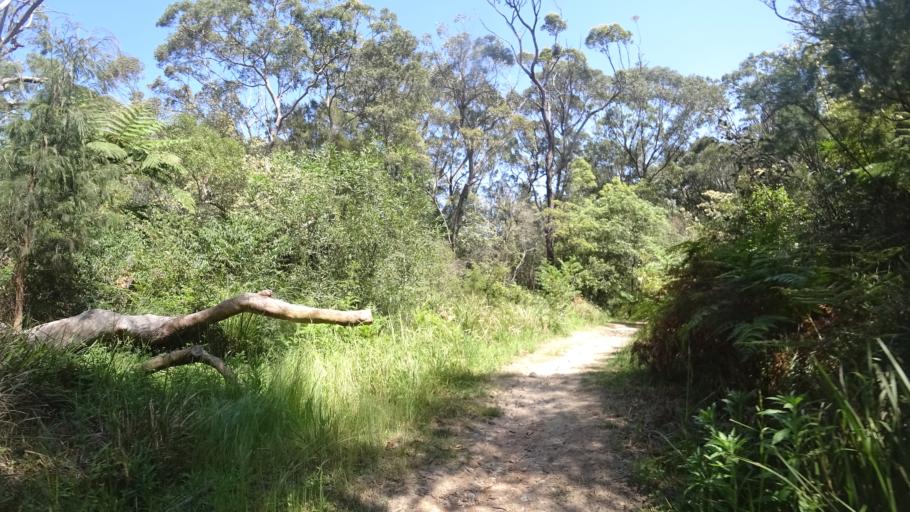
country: AU
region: New South Wales
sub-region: City of Sydney
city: North Turramurra
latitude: -33.6733
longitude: 151.1884
